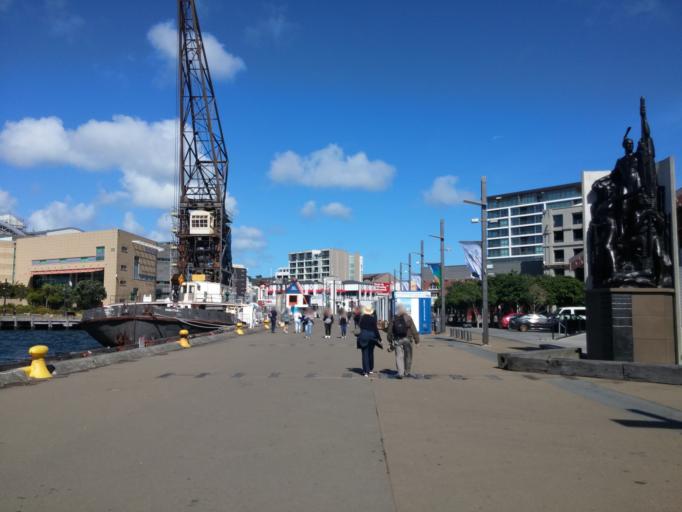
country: NZ
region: Wellington
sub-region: Wellington City
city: Wellington
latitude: -41.2887
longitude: 174.7801
